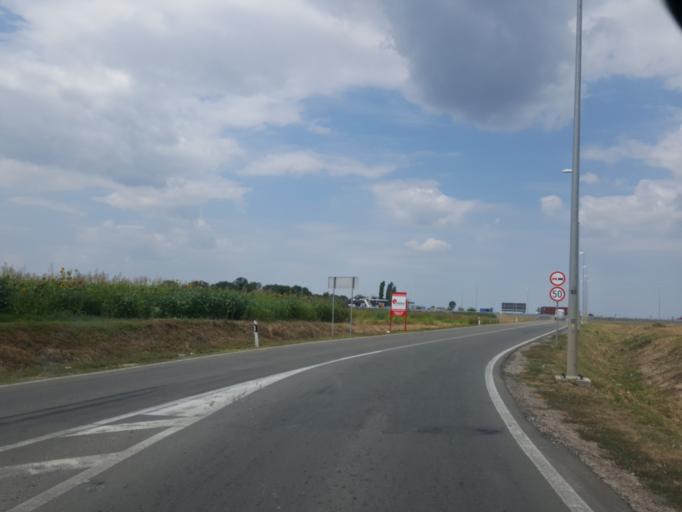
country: RS
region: Autonomna Pokrajina Vojvodina
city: Nova Pazova
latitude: 44.9671
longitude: 20.2348
